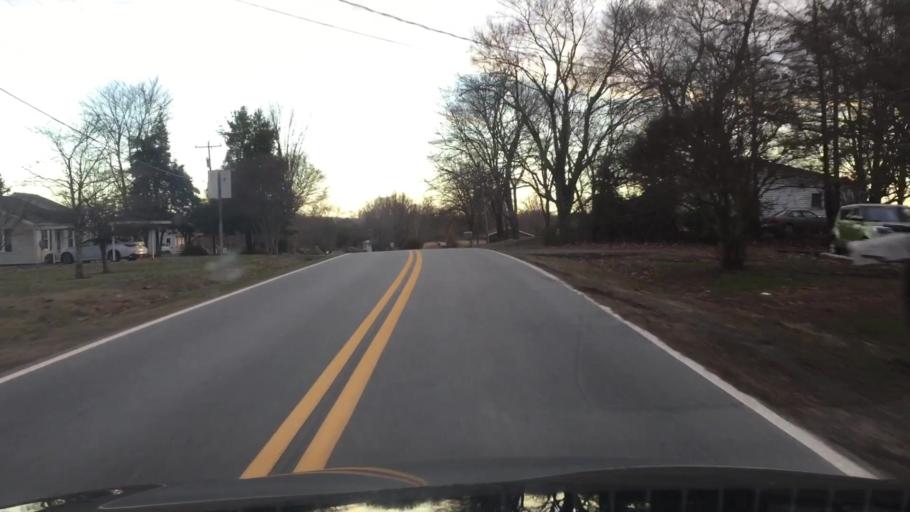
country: US
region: North Carolina
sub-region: Rockingham County
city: Reidsville
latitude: 36.4094
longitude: -79.6577
